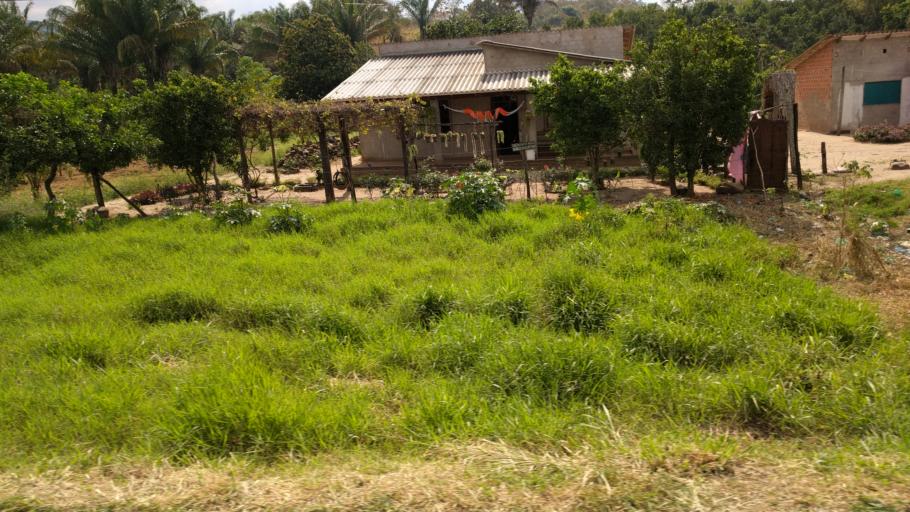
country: BO
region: Santa Cruz
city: Jorochito
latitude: -18.1521
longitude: -63.4924
